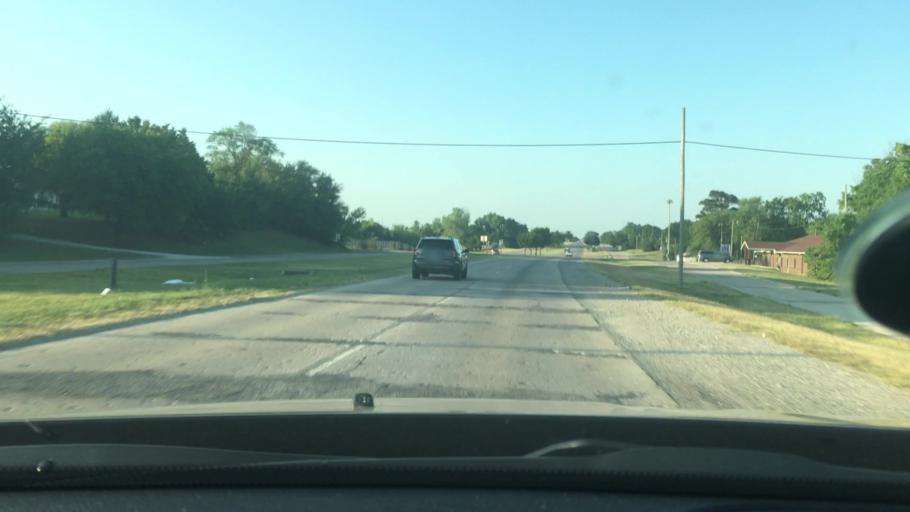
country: US
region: Oklahoma
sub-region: Pontotoc County
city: Ada
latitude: 34.8123
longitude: -96.6785
